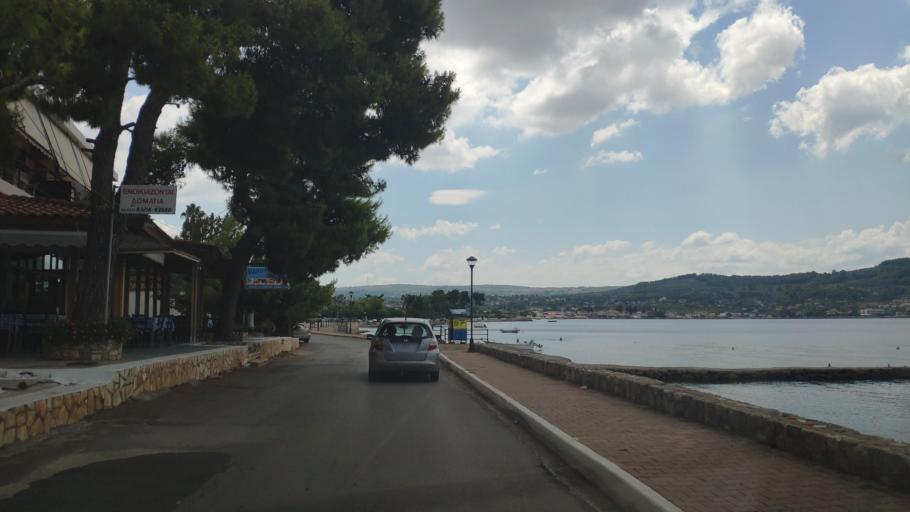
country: GR
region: Central Greece
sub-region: Nomos Fthiotidos
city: Malesina
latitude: 38.6611
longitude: 23.1852
